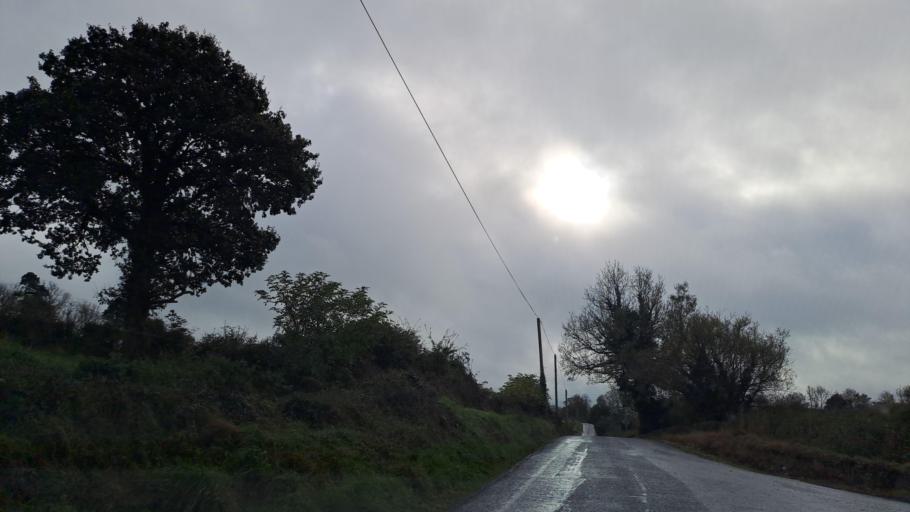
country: IE
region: Ulster
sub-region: An Cabhan
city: Bailieborough
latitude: 53.9481
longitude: -6.9828
